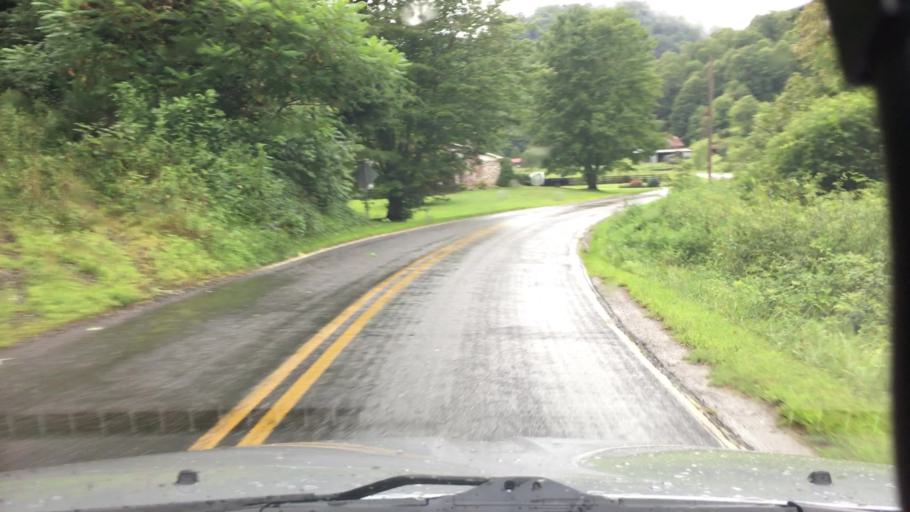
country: US
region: North Carolina
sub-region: Madison County
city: Mars Hill
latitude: 35.9109
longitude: -82.4745
